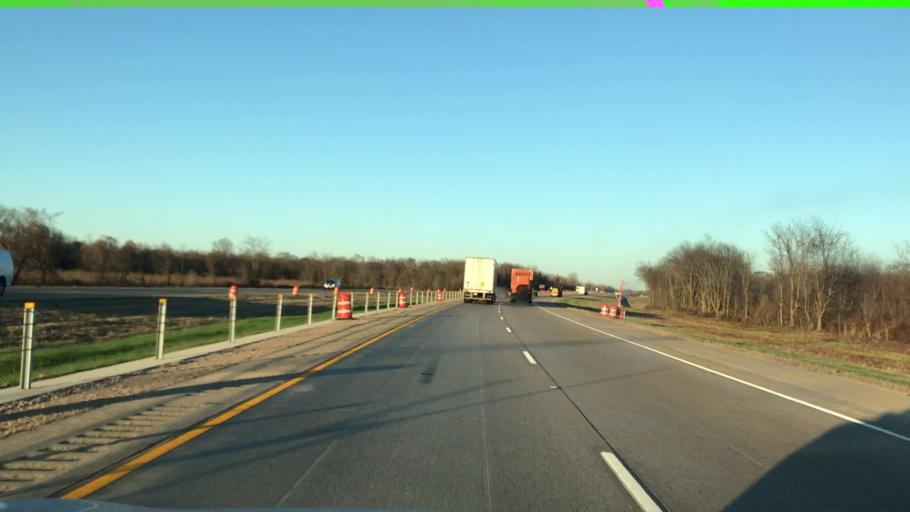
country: US
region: Arkansas
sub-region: Miller County
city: Texarkana
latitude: 33.5837
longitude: -93.8415
